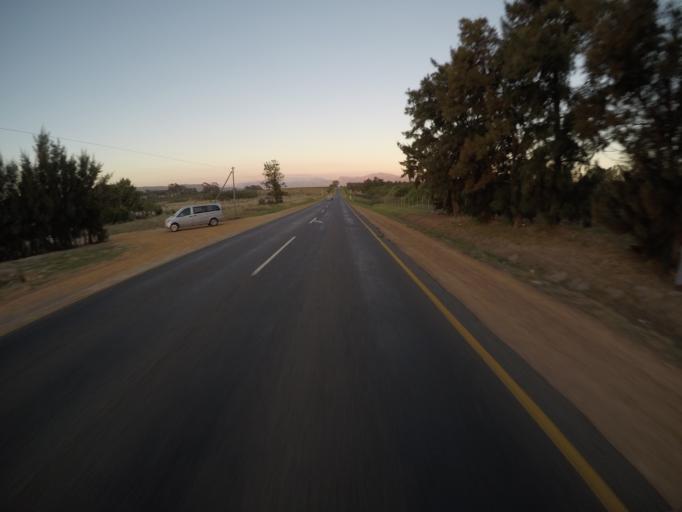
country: ZA
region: Western Cape
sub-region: Cape Winelands District Municipality
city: Paarl
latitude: -33.8068
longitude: 18.8780
